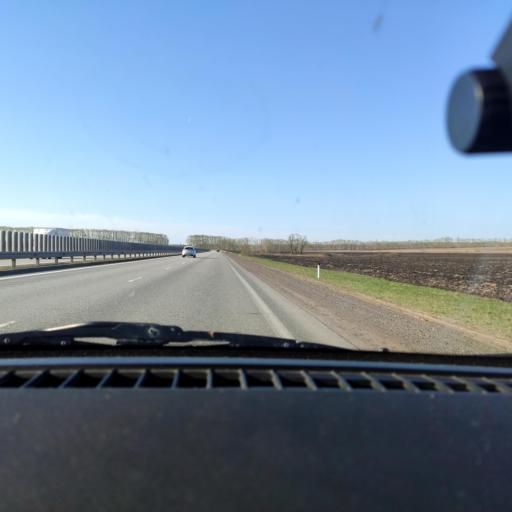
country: RU
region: Bashkortostan
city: Asanovo
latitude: 54.9342
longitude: 55.5780
